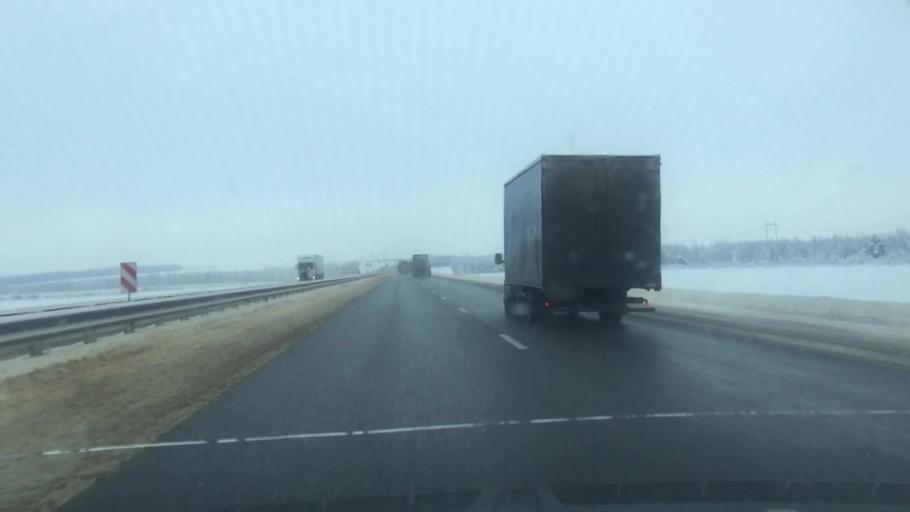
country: RU
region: Lipetsk
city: Yelets
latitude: 52.7402
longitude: 38.4808
